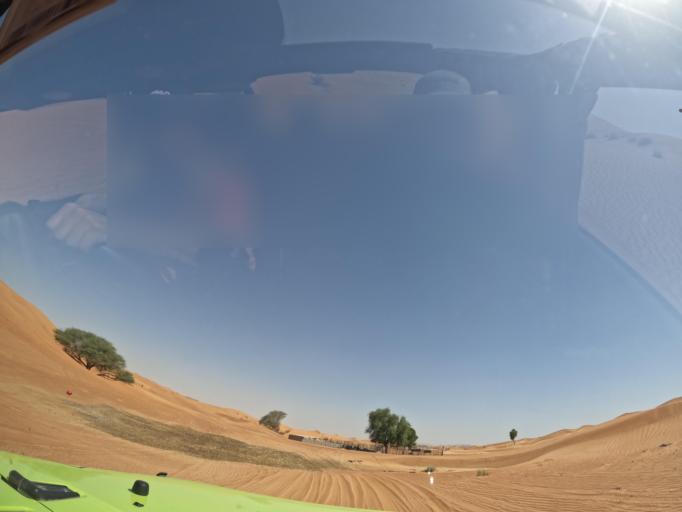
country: AE
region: Ash Shariqah
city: Adh Dhayd
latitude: 24.9899
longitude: 55.7238
